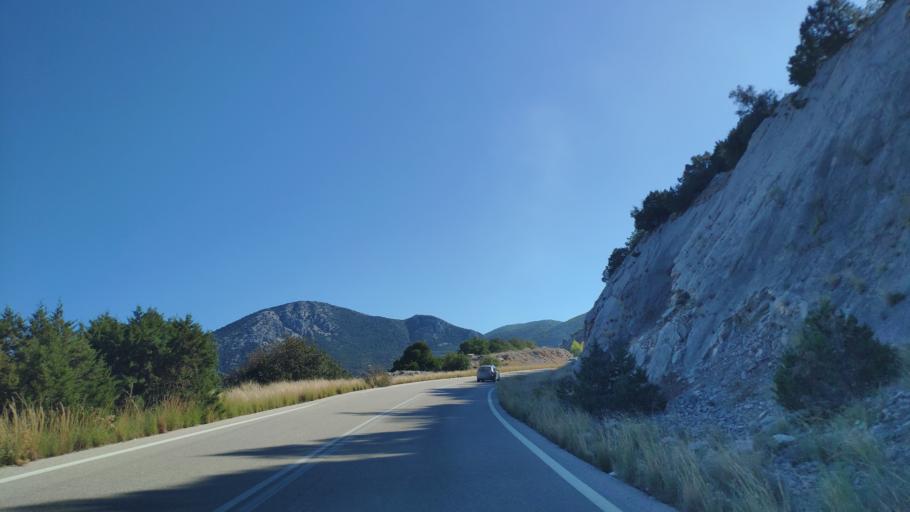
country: GR
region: Peloponnese
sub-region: Nomos Argolidos
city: Palaia Epidavros
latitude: 37.6186
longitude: 23.1487
